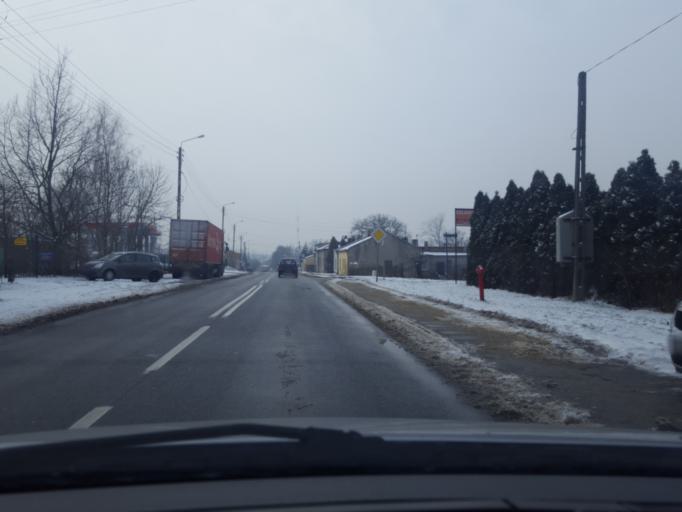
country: PL
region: Lodz Voivodeship
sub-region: Powiat brzezinski
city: Brzeziny
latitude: 51.8082
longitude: 19.7586
